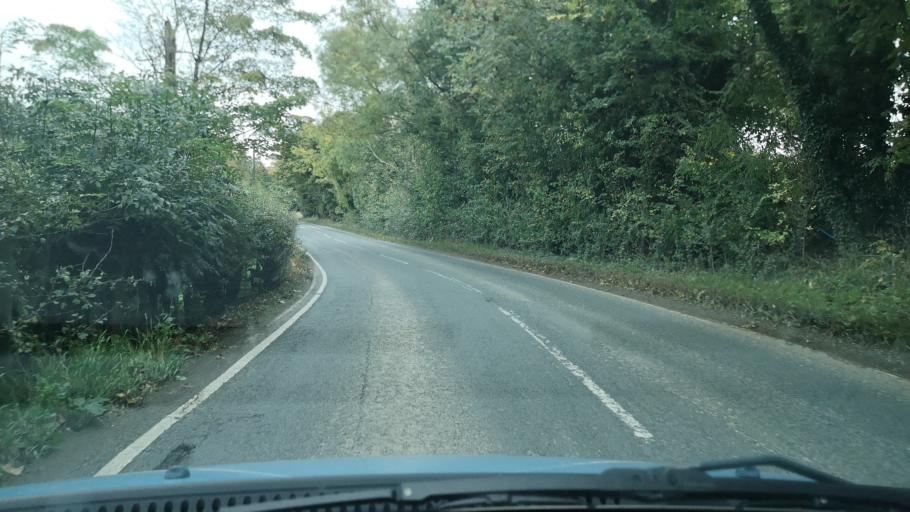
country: GB
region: England
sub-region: City and Borough of Wakefield
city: Fitzwilliam
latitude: 53.6399
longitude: -1.3785
